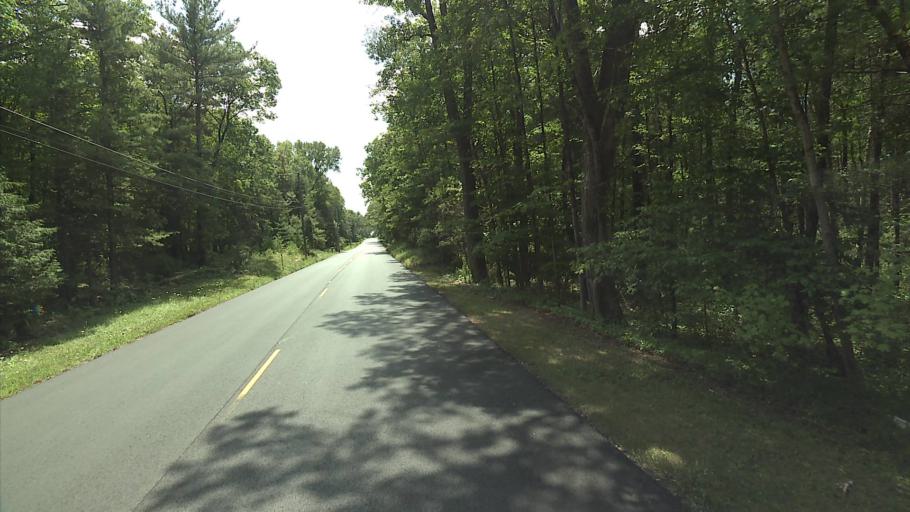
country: US
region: Connecticut
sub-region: Litchfield County
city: Canaan
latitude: 41.9899
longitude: -73.3612
